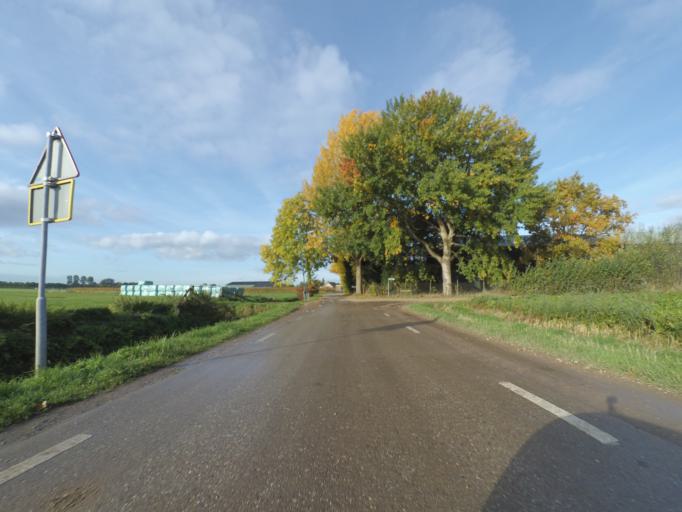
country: NL
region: Utrecht
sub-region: Gemeente Wijk bij Duurstede
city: Wijk bij Duurstede
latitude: 51.9835
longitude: 5.2895
